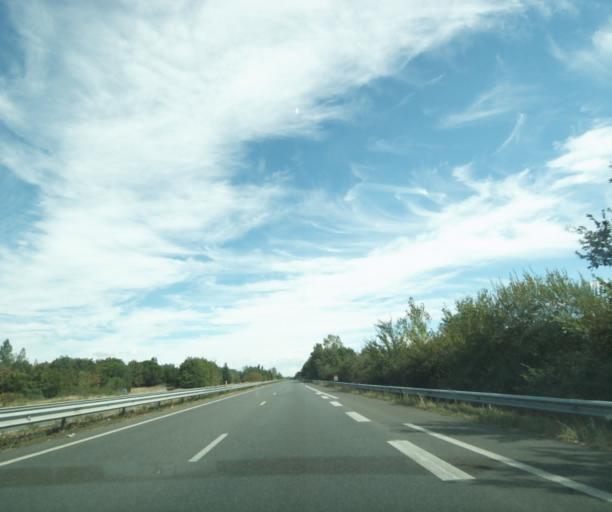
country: FR
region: Midi-Pyrenees
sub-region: Departement du Tarn-et-Garonne
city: Saint-Nicolas-de-la-Grave
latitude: 44.0411
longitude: 1.0159
